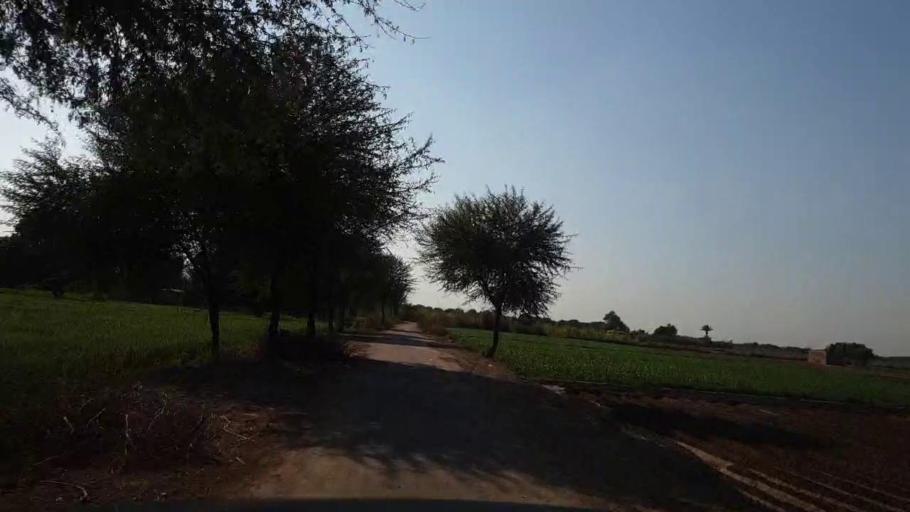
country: PK
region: Sindh
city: Tando Allahyar
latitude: 25.4806
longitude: 68.6585
